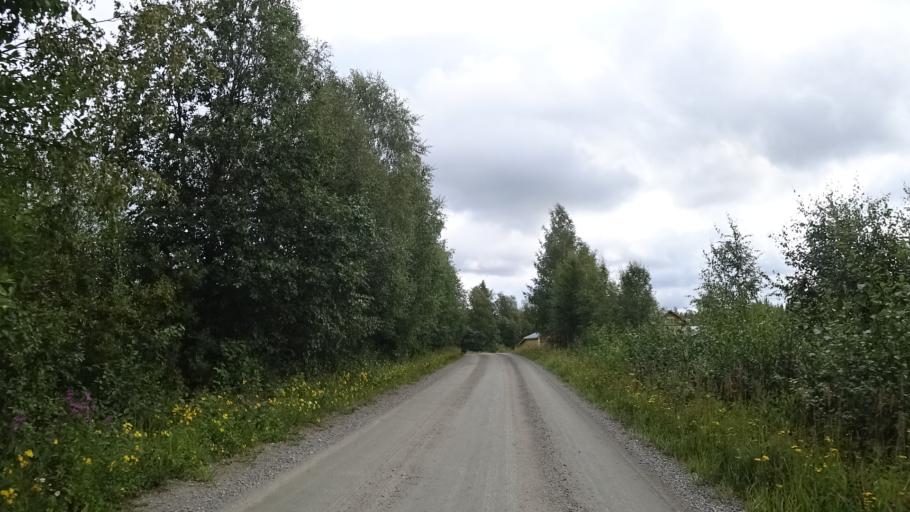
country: FI
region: North Karelia
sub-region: Joensuu
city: Ilomantsi
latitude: 62.9337
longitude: 31.2988
